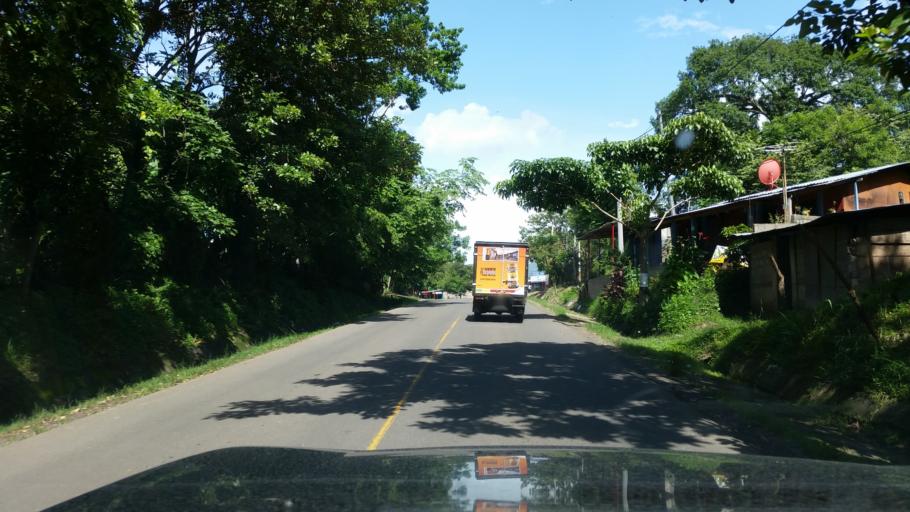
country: NI
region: Matagalpa
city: San Ramon
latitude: 13.0063
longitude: -85.8091
